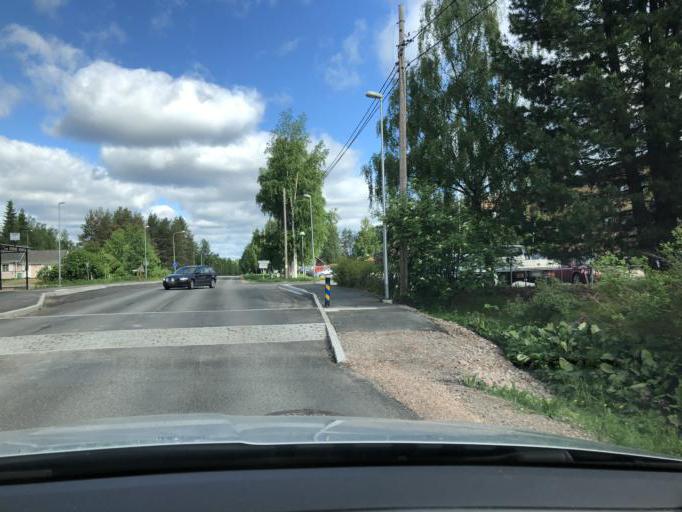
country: SE
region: Norrbotten
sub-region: Pajala Kommun
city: Pajala
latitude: 67.2226
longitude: 23.3436
